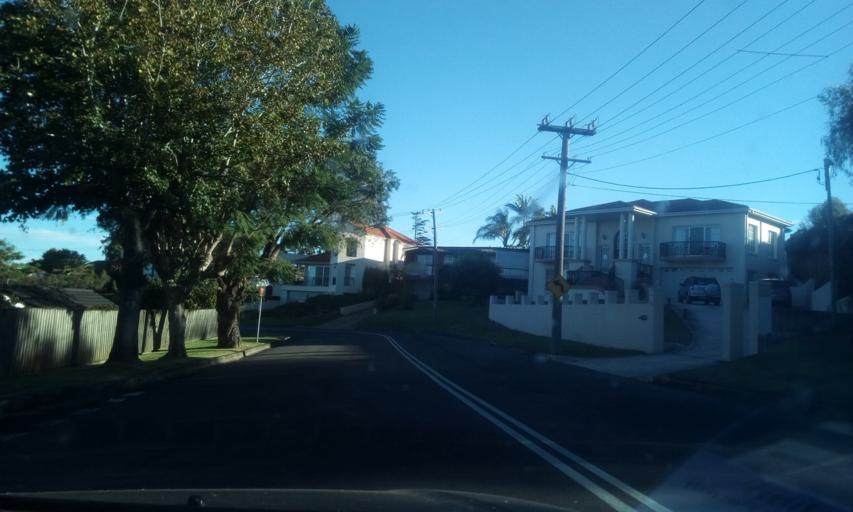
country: AU
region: New South Wales
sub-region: Wollongong
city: Keiraville
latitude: -34.4161
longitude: 150.8612
